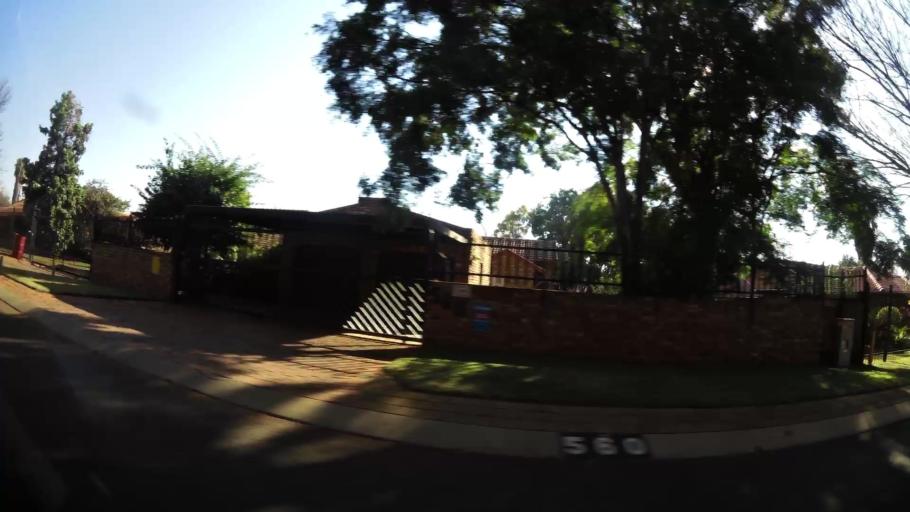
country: ZA
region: Gauteng
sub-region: City of Tshwane Metropolitan Municipality
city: Pretoria
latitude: -25.6504
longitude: 28.2412
